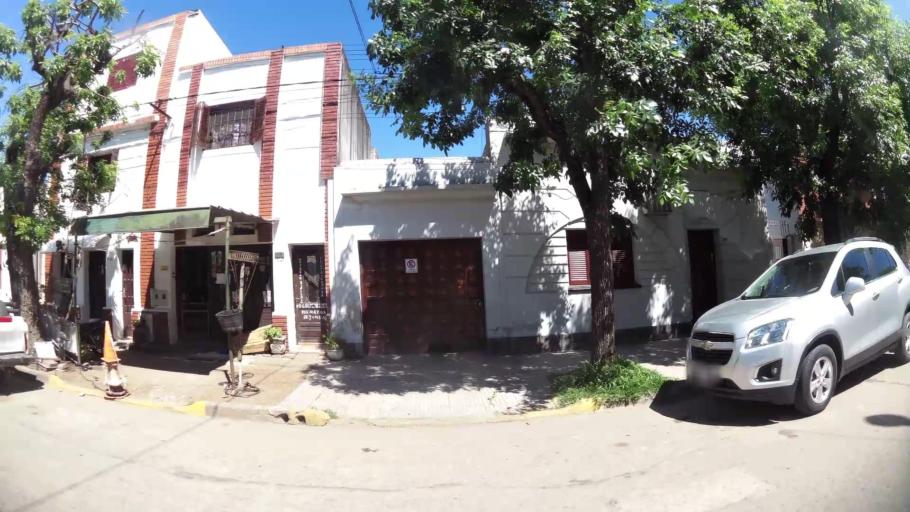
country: AR
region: Santa Fe
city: Esperanza
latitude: -31.4439
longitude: -60.9267
